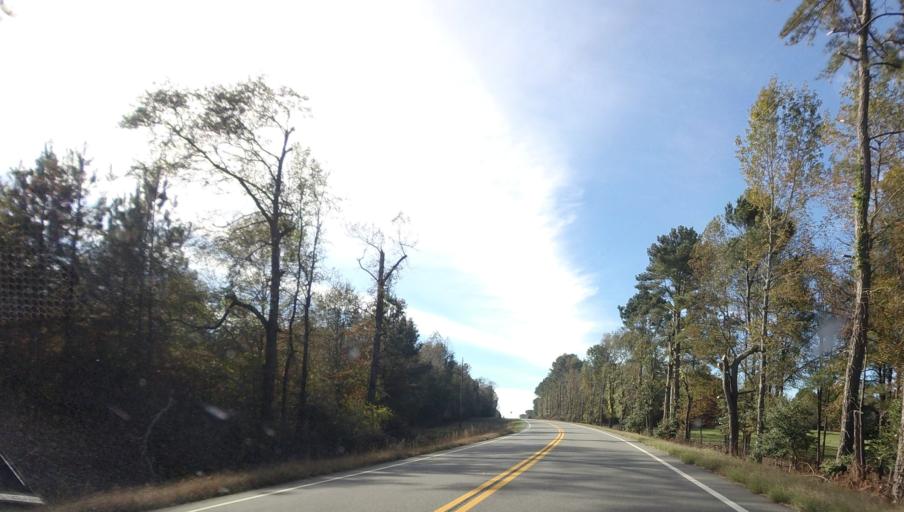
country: US
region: Georgia
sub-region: Upson County
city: Thomaston
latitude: 32.7202
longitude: -84.3139
